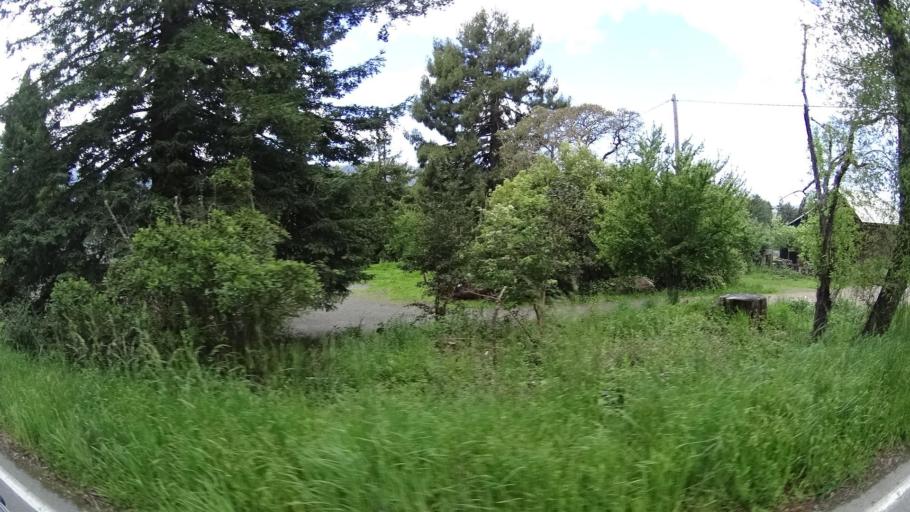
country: US
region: California
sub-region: Humboldt County
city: Blue Lake
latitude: 40.8761
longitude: -123.9797
